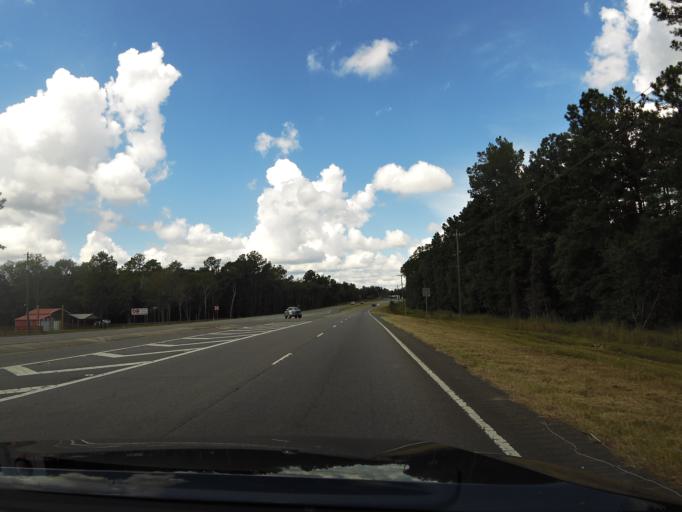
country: US
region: Georgia
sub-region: Charlton County
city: Folkston
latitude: 30.8052
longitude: -81.9934
